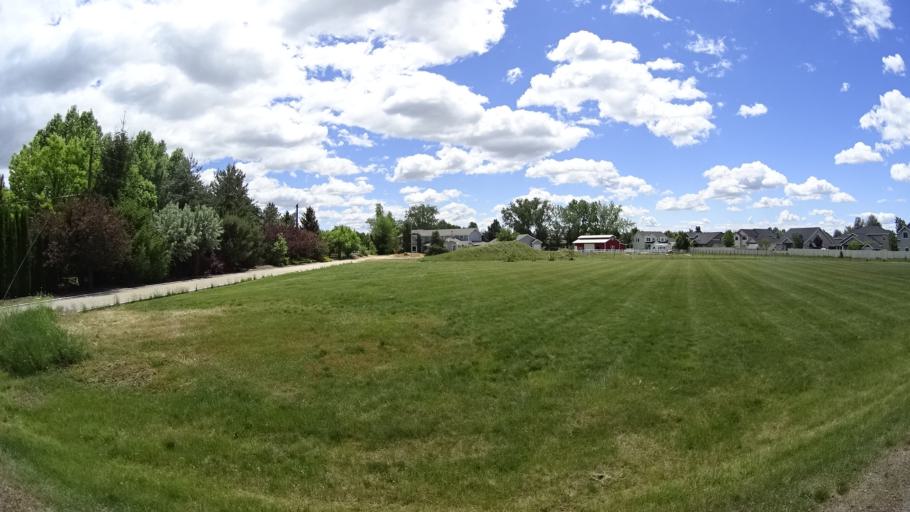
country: US
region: Idaho
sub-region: Ada County
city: Eagle
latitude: 43.6448
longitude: -116.3382
